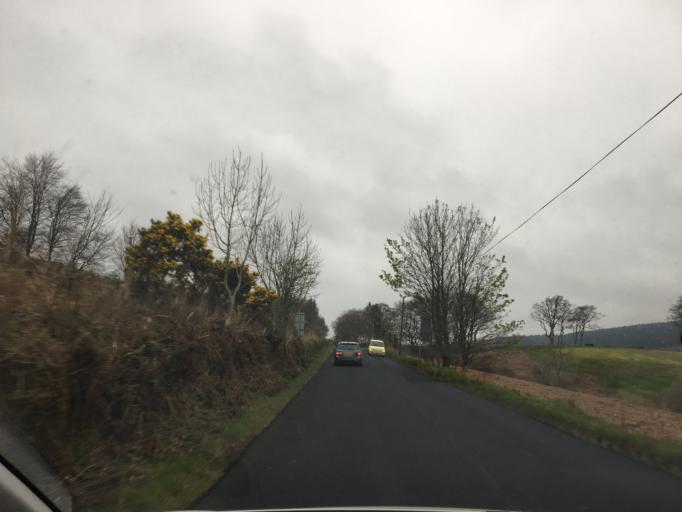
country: GB
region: Scotland
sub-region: North Ayrshire
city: Lamlash
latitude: 55.5427
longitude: -5.1294
